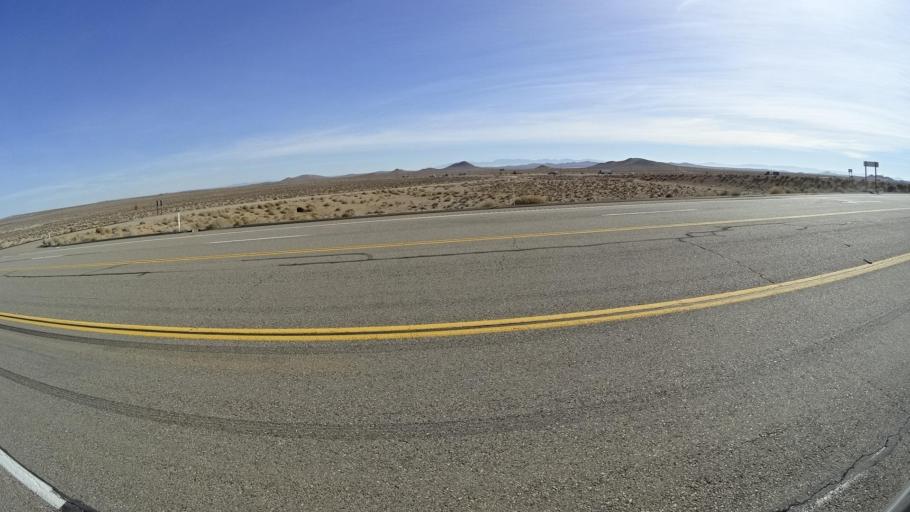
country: US
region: California
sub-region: Kern County
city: Mojave
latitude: 35.0395
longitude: -118.1048
